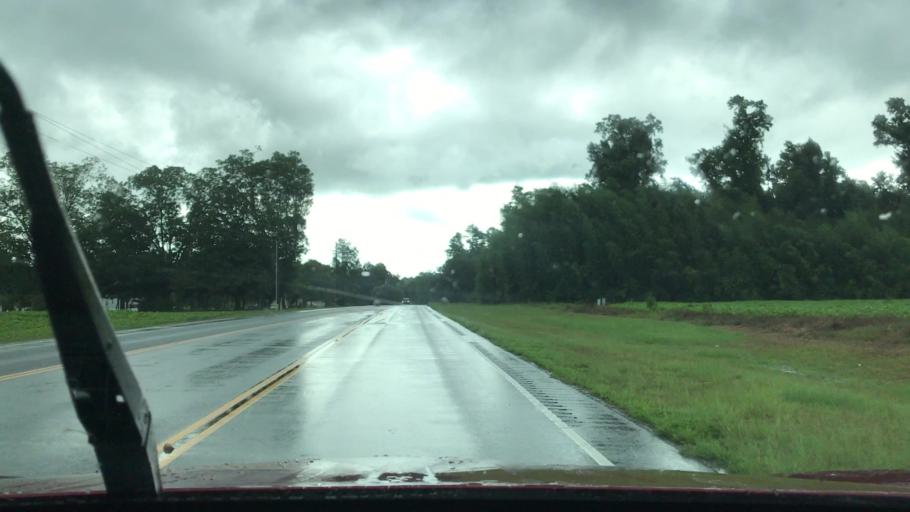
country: US
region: South Carolina
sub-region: Horry County
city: Loris
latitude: 33.9047
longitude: -78.8521
